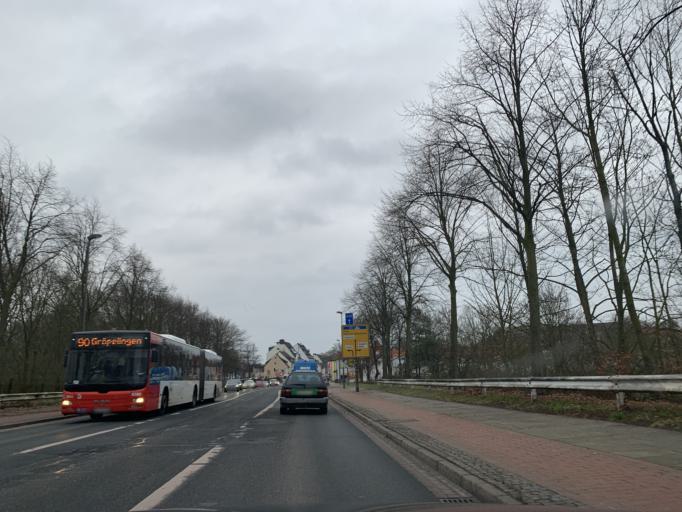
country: DE
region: Lower Saxony
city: Ritterhude
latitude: 53.1658
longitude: 8.7024
